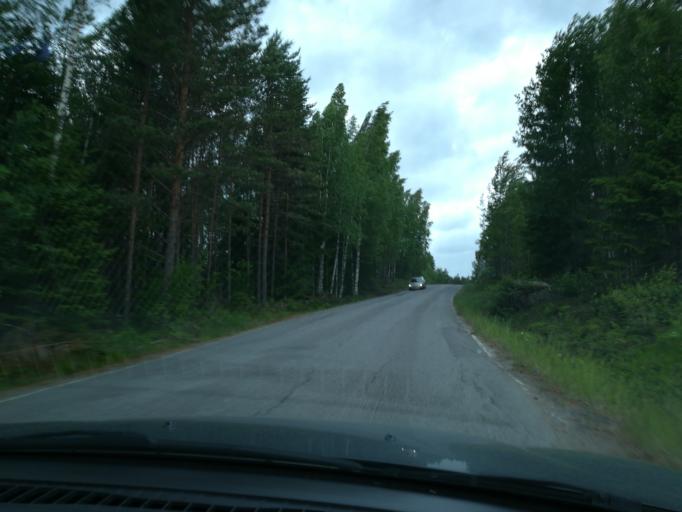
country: FI
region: South Karelia
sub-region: Lappeenranta
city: Savitaipale
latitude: 61.3208
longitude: 27.4894
